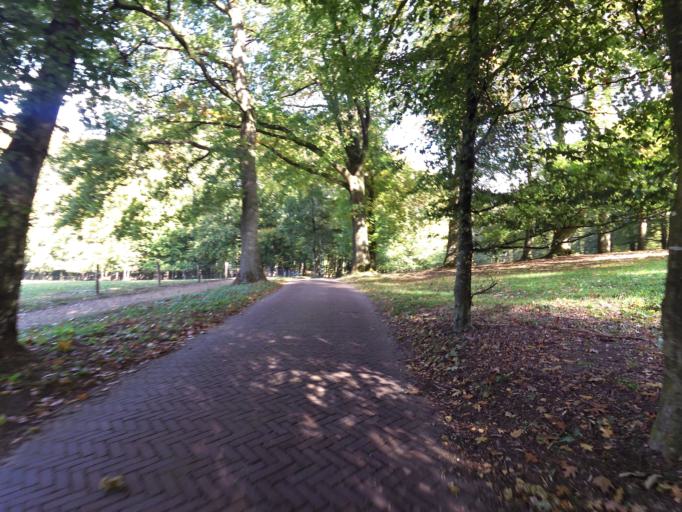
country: NL
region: Gelderland
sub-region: Gemeente Rheden
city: Rheden
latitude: 52.0185
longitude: 6.0198
